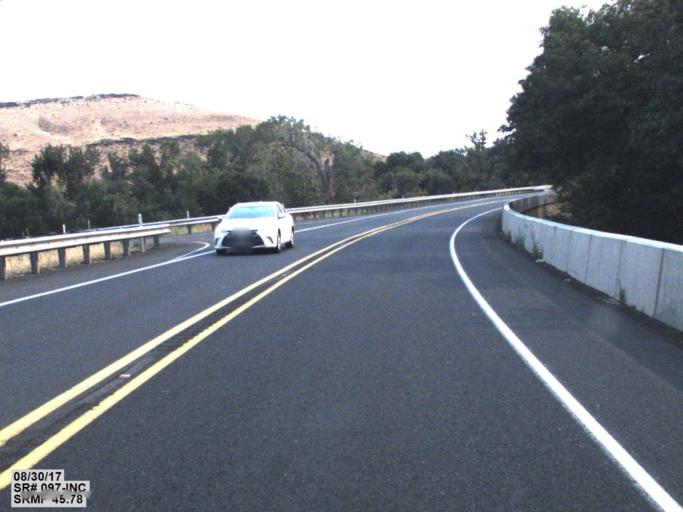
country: US
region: Washington
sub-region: Yakima County
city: Toppenish
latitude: 46.2035
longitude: -120.4799
